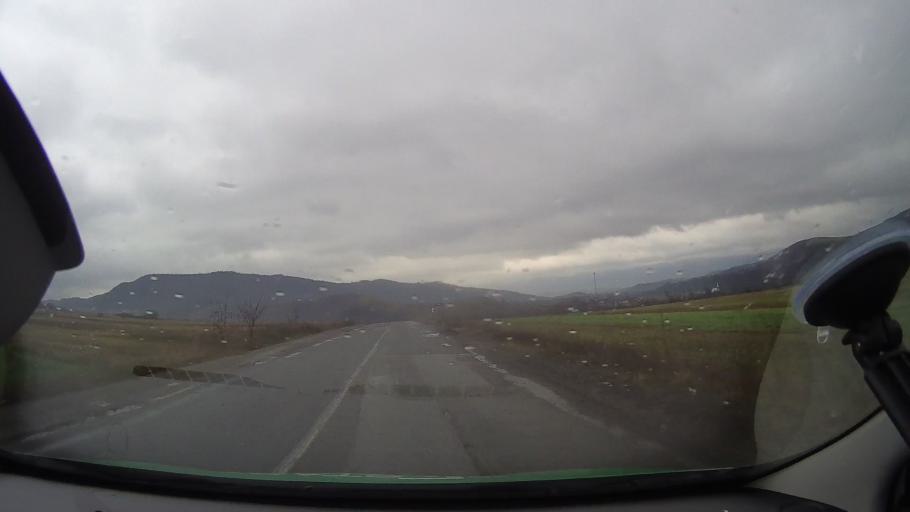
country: RO
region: Arad
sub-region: Comuna Halmagiu
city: Halmagiu
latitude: 46.2327
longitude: 22.5594
